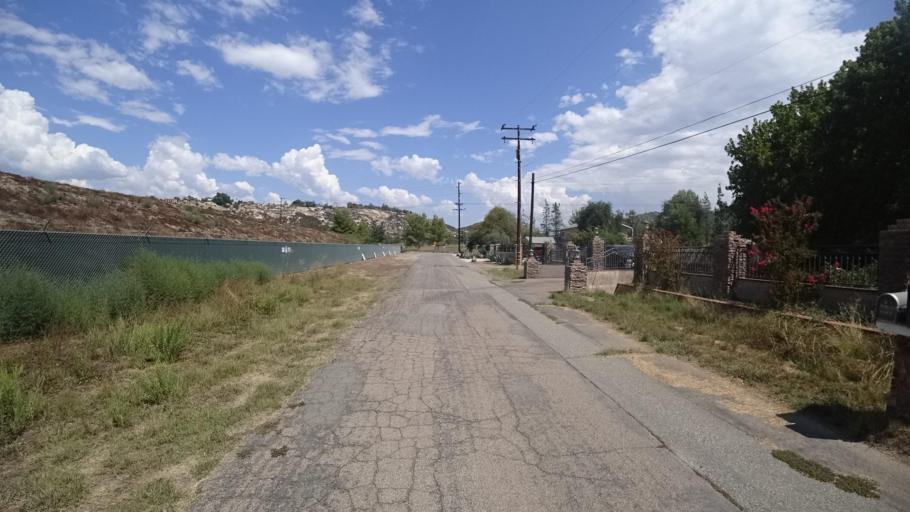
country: US
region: California
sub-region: San Diego County
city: Valley Center
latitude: 33.2101
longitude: -117.0281
